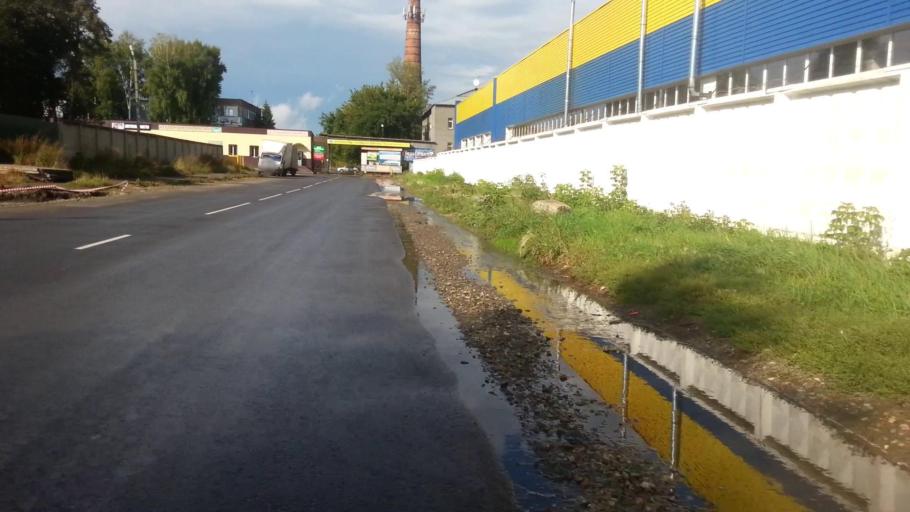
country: RU
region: Altai Krai
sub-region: Gorod Barnaulskiy
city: Barnaul
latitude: 53.3434
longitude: 83.7230
